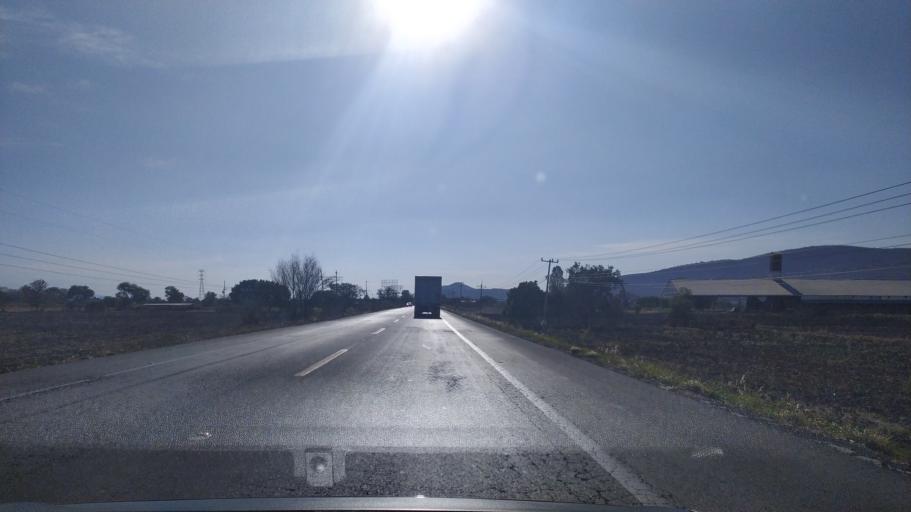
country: MX
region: Jalisco
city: Jamay
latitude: 20.2937
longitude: -102.6508
